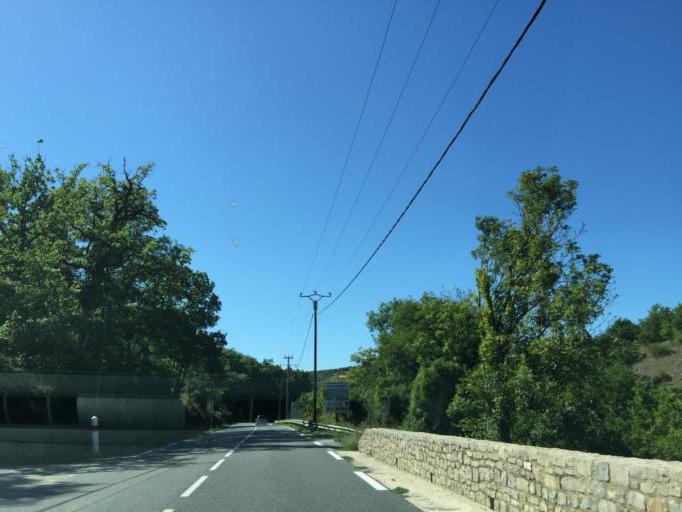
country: FR
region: Midi-Pyrenees
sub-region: Departement de l'Aveyron
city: Saint-Georges-de-Luzencon
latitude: 44.0112
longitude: 2.9707
